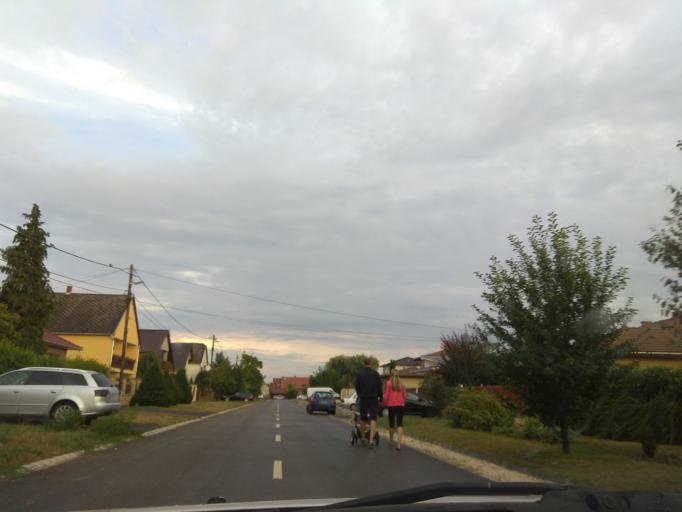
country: HU
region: Borsod-Abauj-Zemplen
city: Miskolc
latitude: 48.0742
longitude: 20.8198
